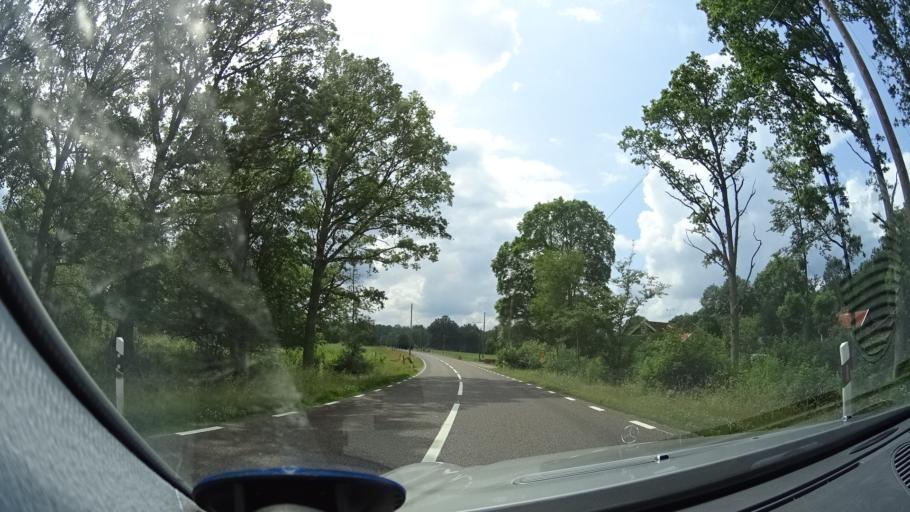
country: SE
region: Kalmar
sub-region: Emmaboda Kommun
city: Emmaboda
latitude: 56.6325
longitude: 15.6497
